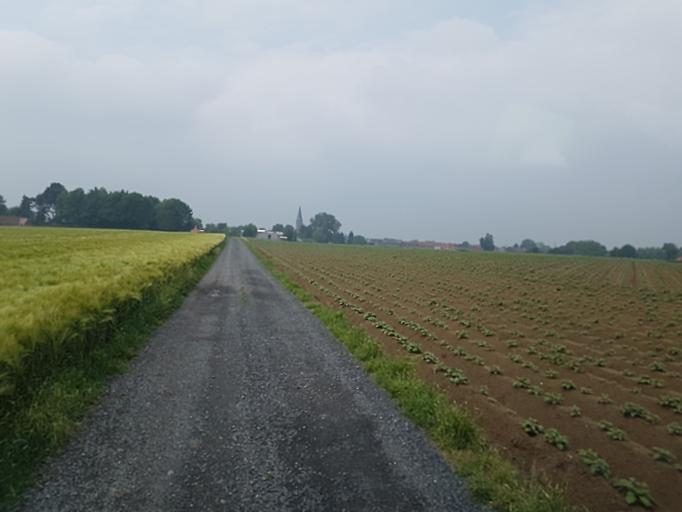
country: BE
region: Flanders
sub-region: Provincie West-Vlaanderen
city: Avelgem
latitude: 50.8156
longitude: 3.4427
